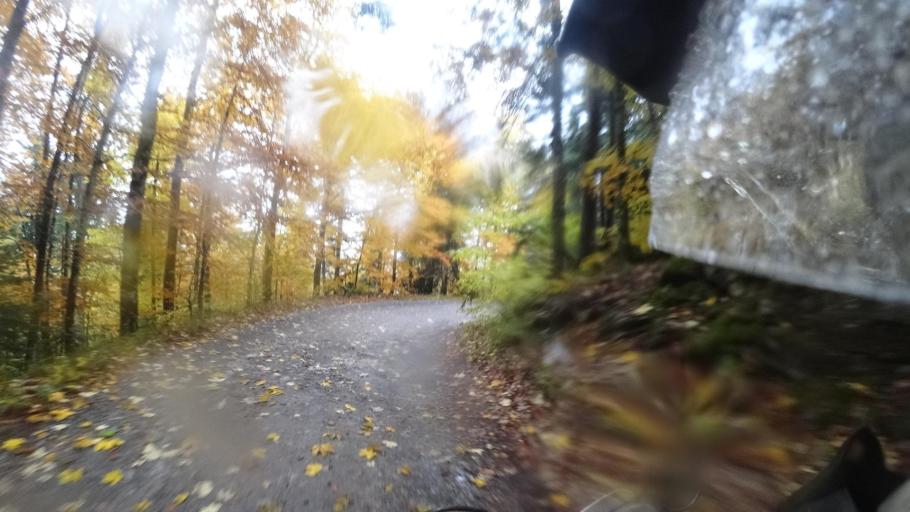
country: HR
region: Primorsko-Goranska
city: Vrbovsko
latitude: 45.3115
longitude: 15.0688
